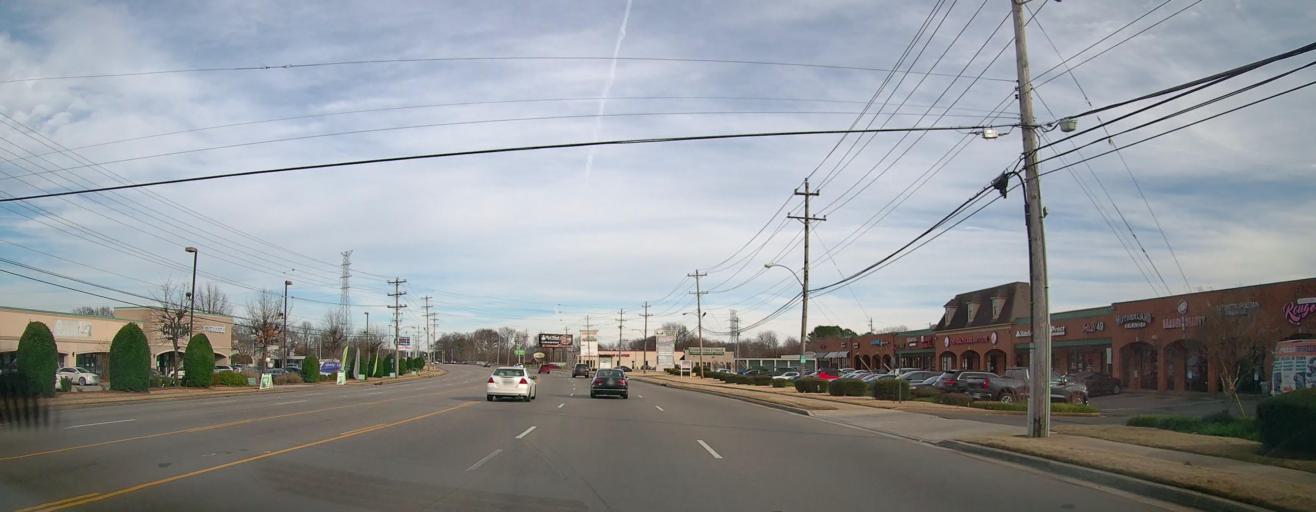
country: US
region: Tennessee
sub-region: Shelby County
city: Germantown
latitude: 35.0489
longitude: -89.8227
